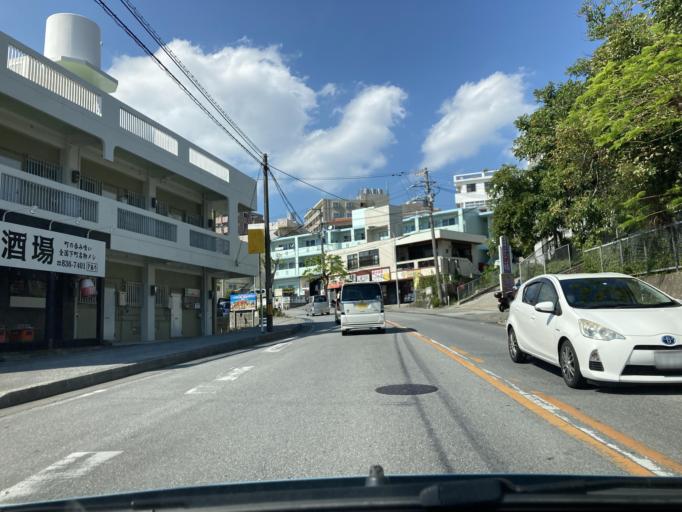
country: JP
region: Okinawa
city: Tomigusuku
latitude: 26.1973
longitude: 127.7035
